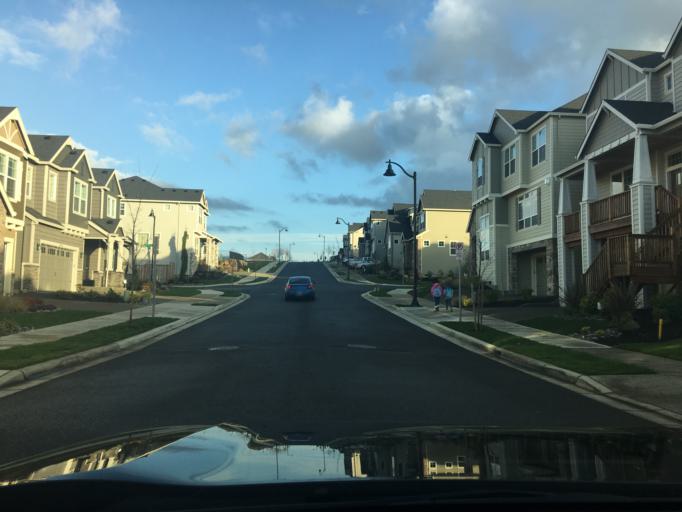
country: US
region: Oregon
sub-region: Washington County
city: Bethany
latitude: 45.5757
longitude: -122.8521
